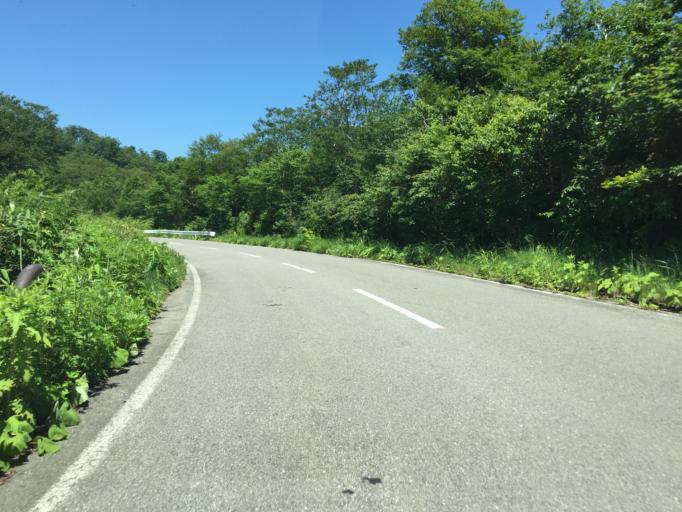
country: JP
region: Fukushima
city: Inawashiro
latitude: 37.6778
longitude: 140.2348
